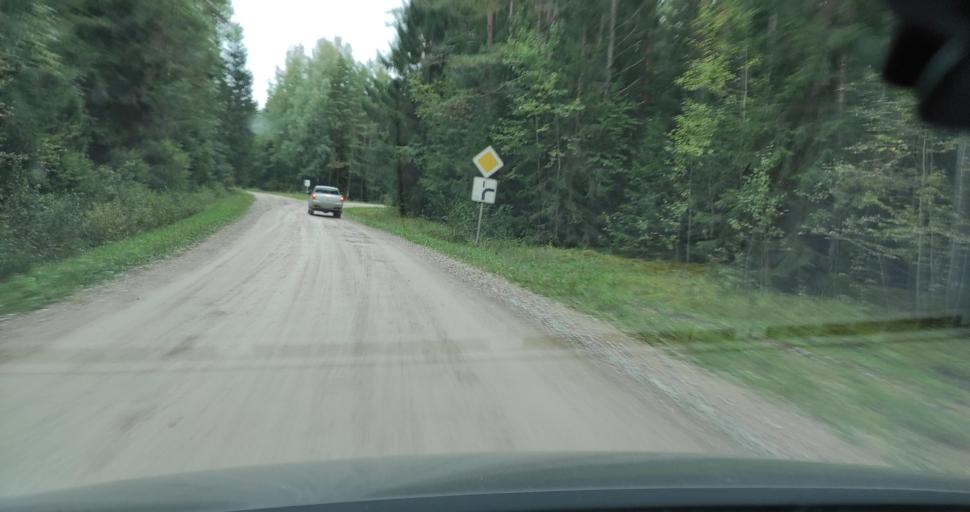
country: LV
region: Talsu Rajons
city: Stende
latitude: 57.0336
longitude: 22.3226
